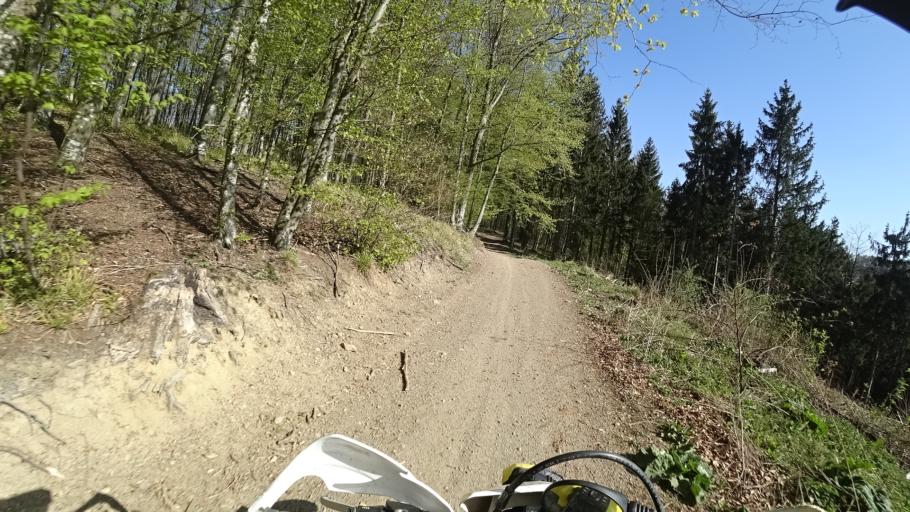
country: HR
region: Zagrebacka
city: Jablanovec
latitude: 45.8960
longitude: 15.9170
